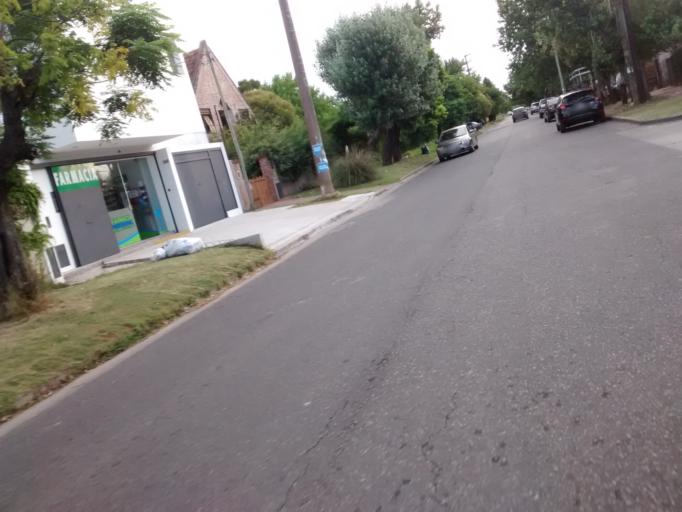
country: AR
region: Buenos Aires
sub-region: Partido de La Plata
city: La Plata
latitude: -34.8712
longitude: -58.0574
